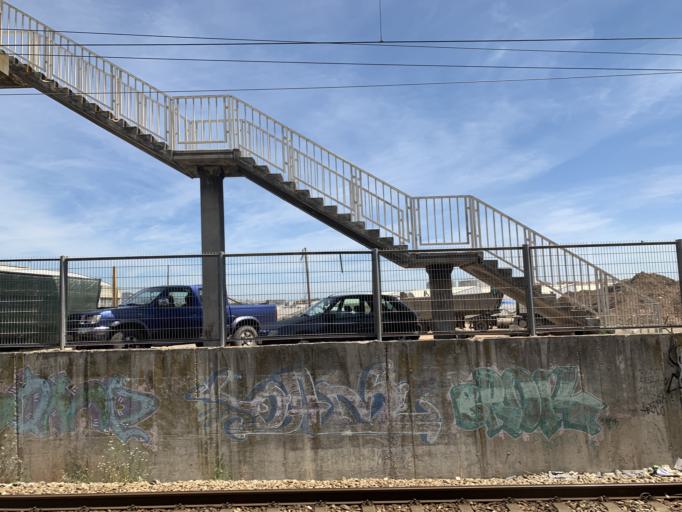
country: PT
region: Lisbon
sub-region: Amadora
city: Amadora
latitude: 38.7493
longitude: -9.2184
